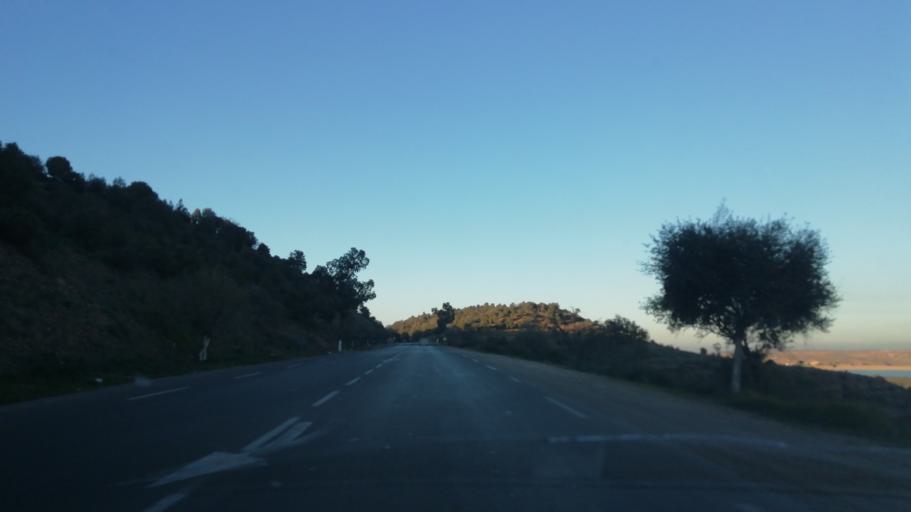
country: DZ
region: Tlemcen
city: Nedroma
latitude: 34.8724
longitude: -1.6689
